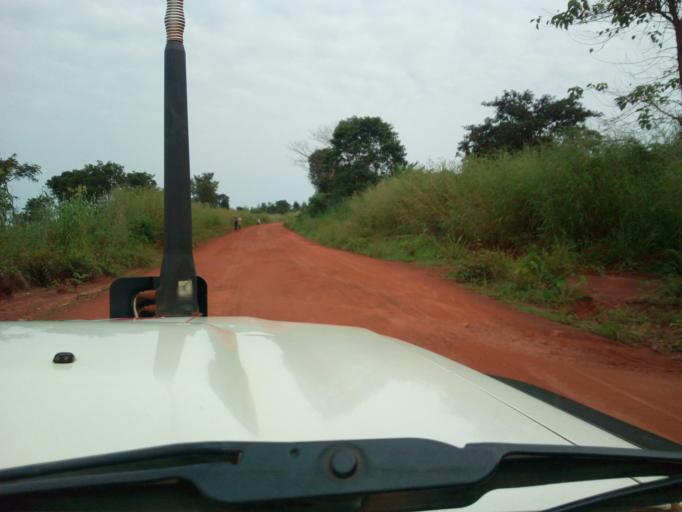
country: CF
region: Ouaka
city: Bambari
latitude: 5.7827
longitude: 20.6437
